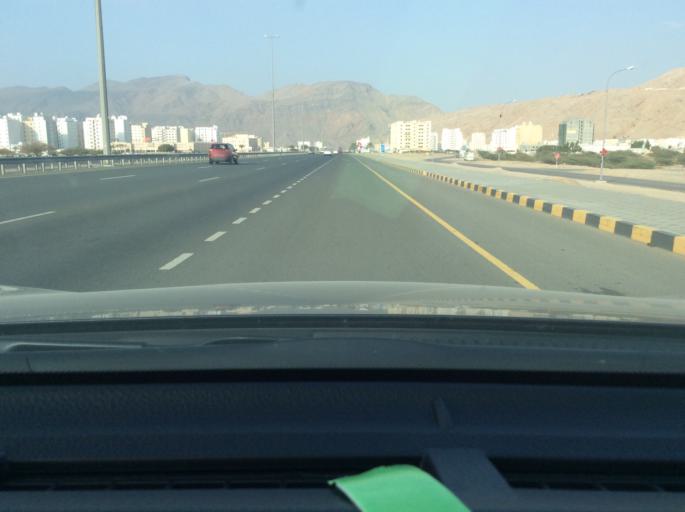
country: OM
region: Muhafazat Masqat
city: Bawshar
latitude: 23.5145
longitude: 58.5032
